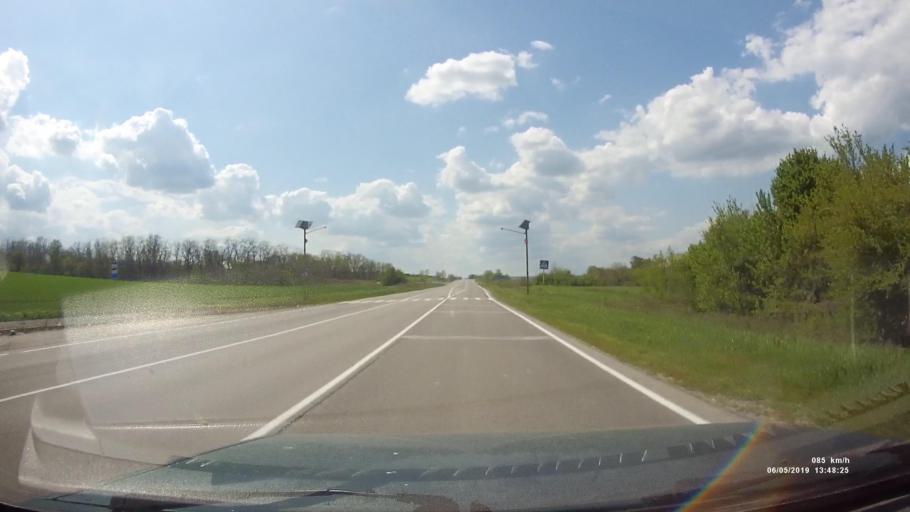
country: RU
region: Rostov
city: Melikhovskaya
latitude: 47.6588
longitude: 40.5438
